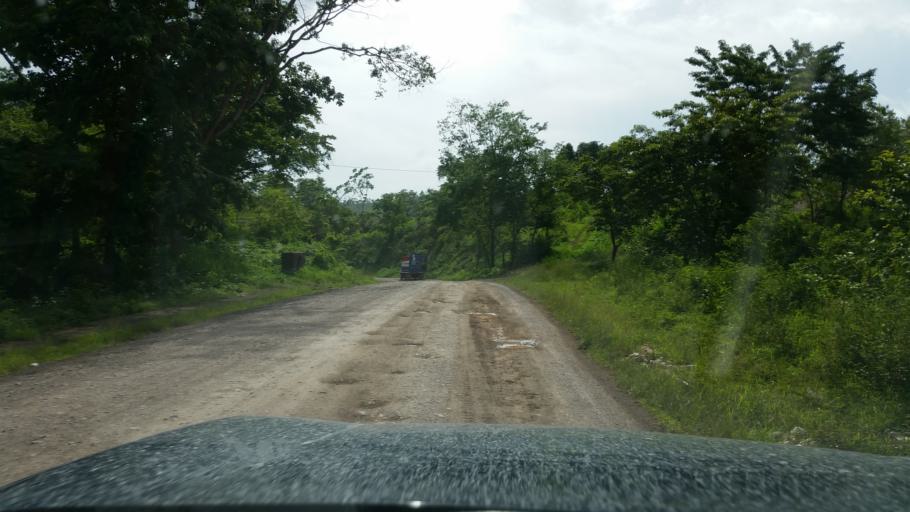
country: NI
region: Atlantico Norte (RAAN)
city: Siuna
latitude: 13.5939
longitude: -84.8093
